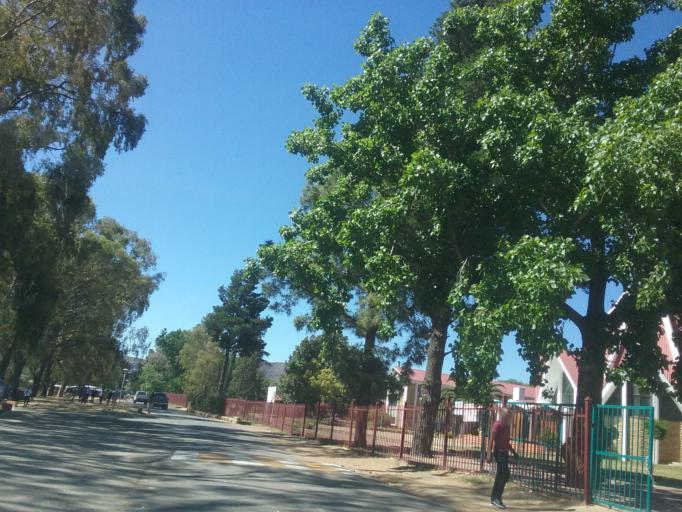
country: LS
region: Maseru
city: Nako
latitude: -29.4502
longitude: 27.7241
